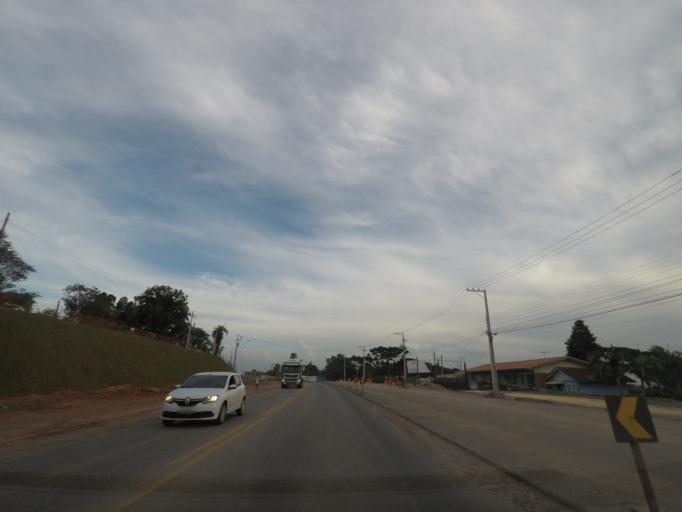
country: BR
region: Parana
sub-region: Colombo
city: Colombo
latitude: -25.3255
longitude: -49.2210
